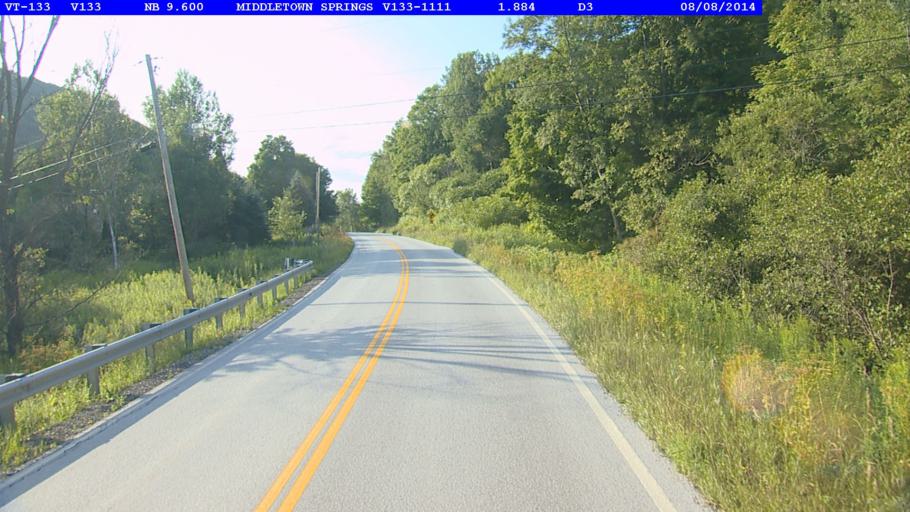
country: US
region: Vermont
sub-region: Rutland County
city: Poultney
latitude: 43.4622
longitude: -73.1116
